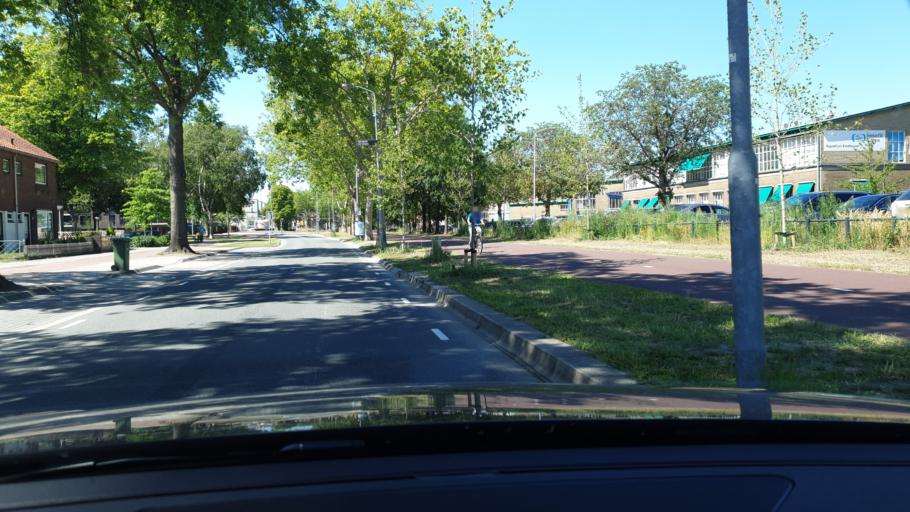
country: NL
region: North Brabant
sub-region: Gemeente Eindhoven
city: Eindhoven
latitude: 51.4489
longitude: 5.4511
